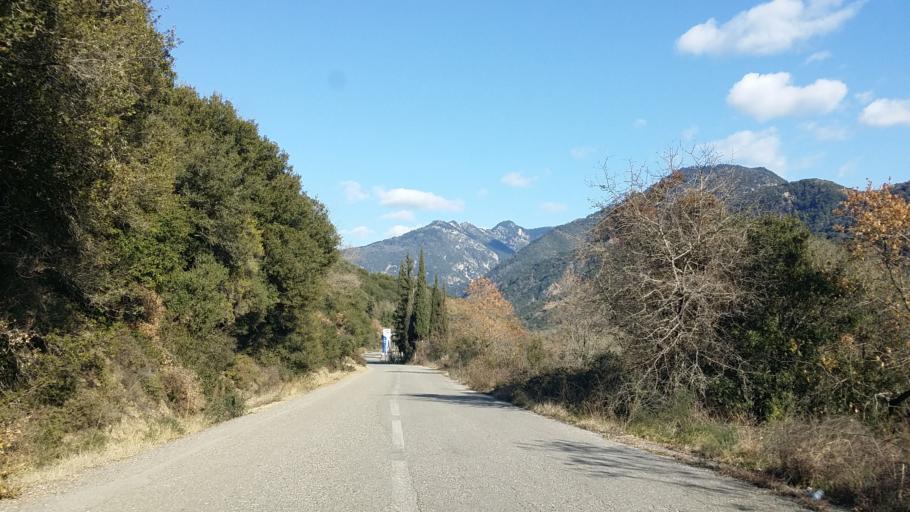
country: GR
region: Central Greece
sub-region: Nomos Evrytanias
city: Kerasochori
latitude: 38.9942
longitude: 21.5636
